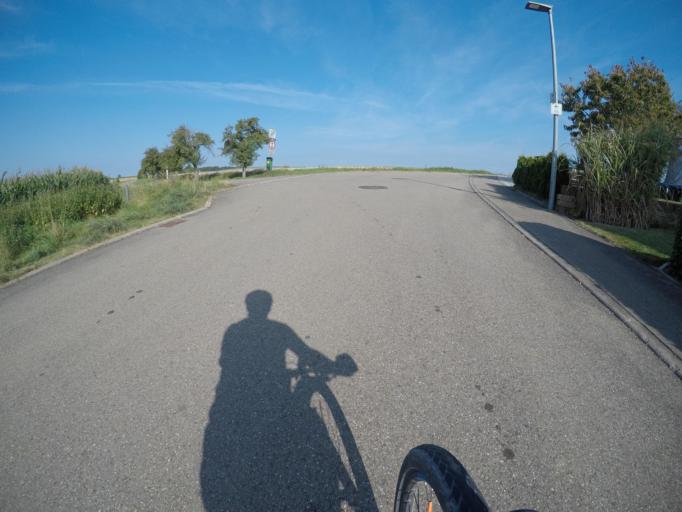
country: DE
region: Baden-Wuerttemberg
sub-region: Regierungsbezirk Stuttgart
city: Gerstetten
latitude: 48.6262
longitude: 10.0013
